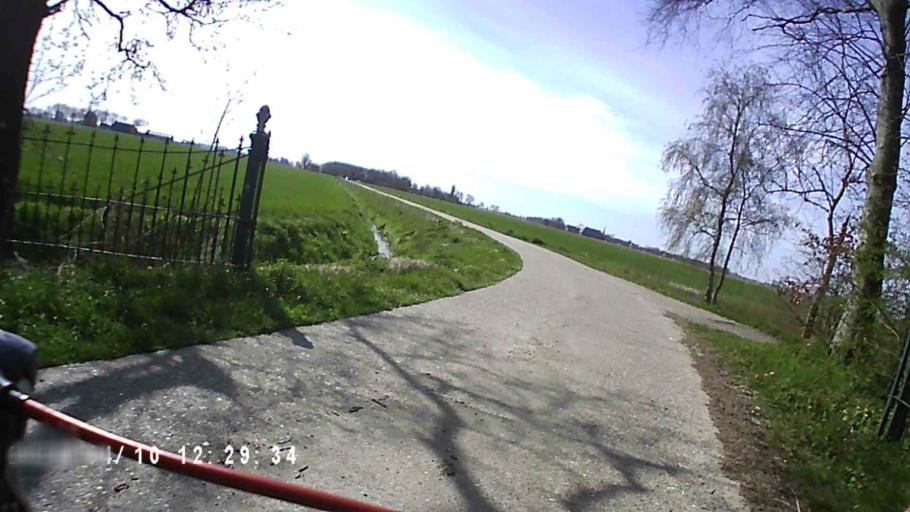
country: NL
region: Groningen
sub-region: Gemeente De Marne
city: Ulrum
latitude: 53.4019
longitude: 6.4103
